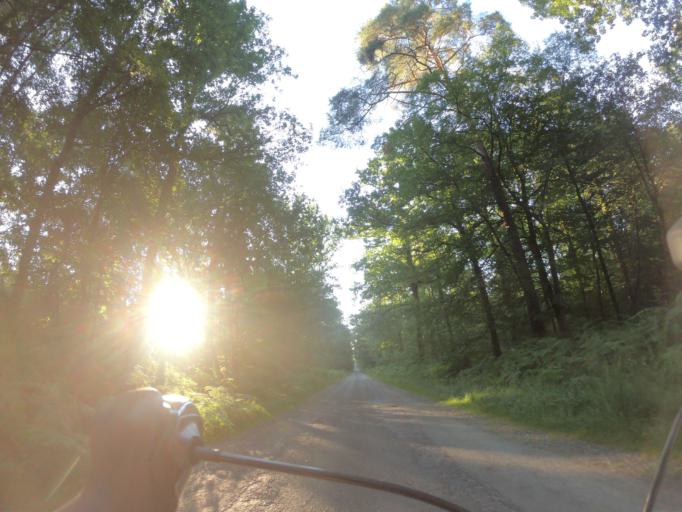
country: FR
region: Lower Normandy
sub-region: Departement de l'Orne
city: Magny-le-Desert
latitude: 48.5393
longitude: -0.3301
